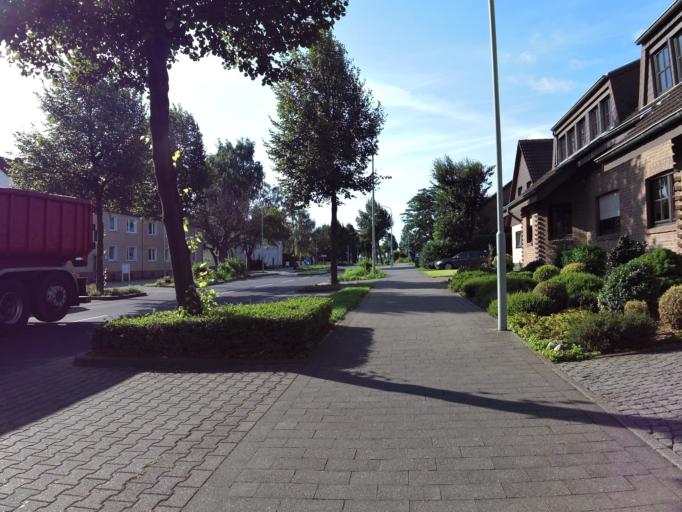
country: DE
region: North Rhine-Westphalia
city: Siersdorf
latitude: 50.8962
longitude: 6.2288
